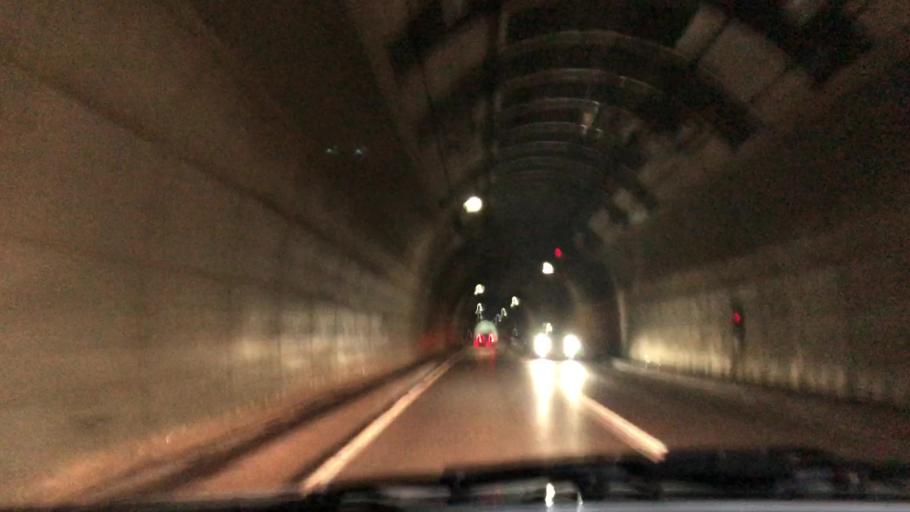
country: JP
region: Hokkaido
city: Iwamizawa
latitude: 42.9218
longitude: 142.1160
